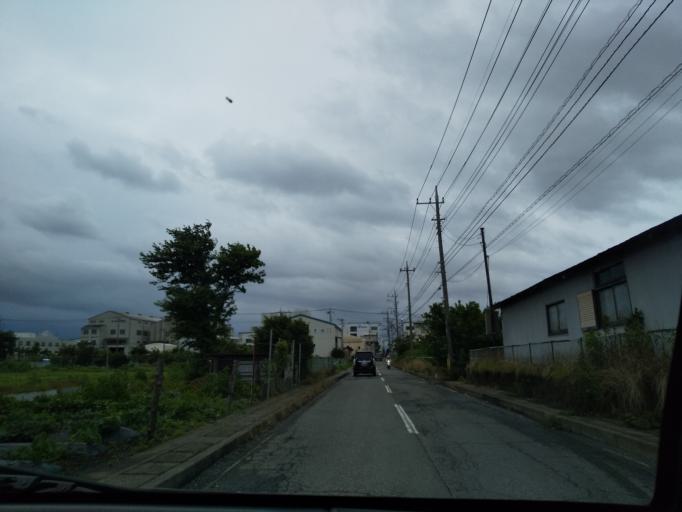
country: JP
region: Kanagawa
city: Minami-rinkan
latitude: 35.4379
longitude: 139.4427
